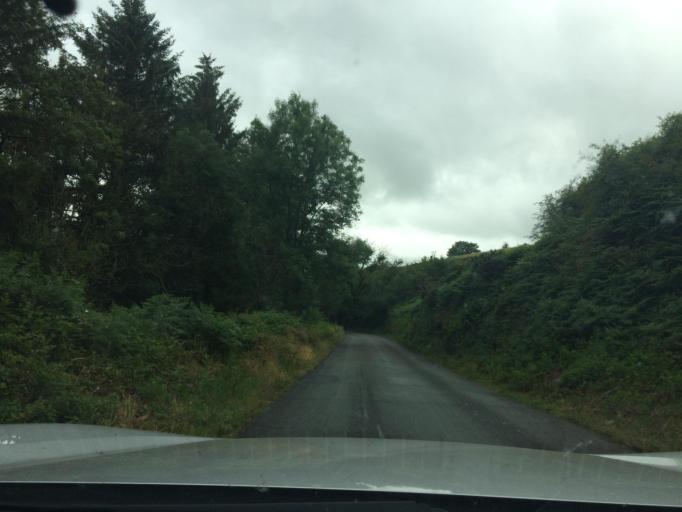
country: IE
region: Munster
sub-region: Waterford
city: Dungarvan
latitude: 52.1951
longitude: -7.7287
